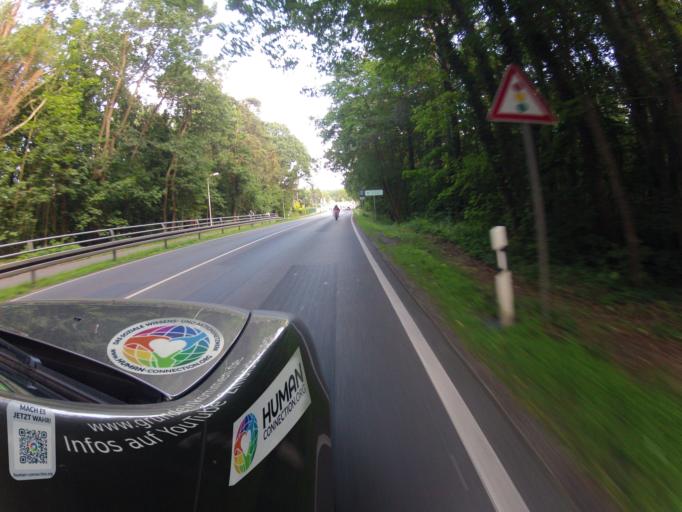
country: DE
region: Mecklenburg-Vorpommern
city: Loddin
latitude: 54.0363
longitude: 14.0197
